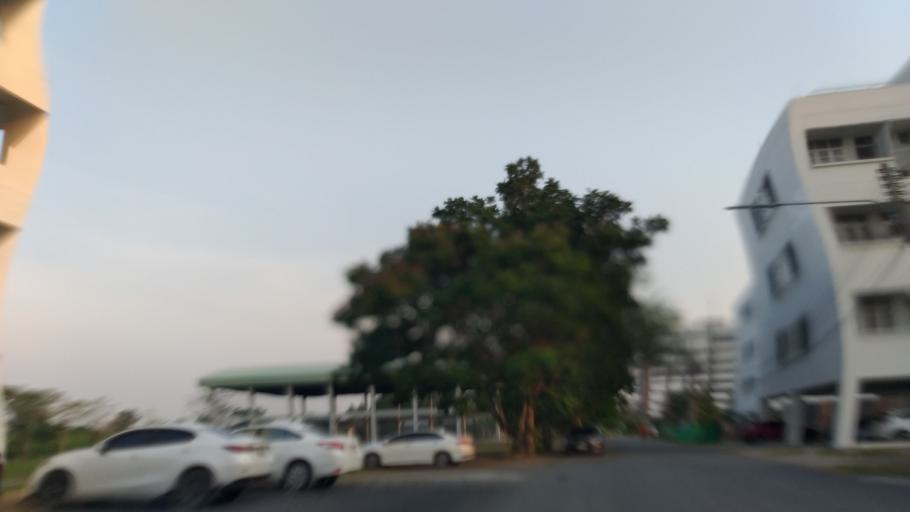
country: TH
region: Pathum Thani
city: Nong Suea
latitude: 14.0716
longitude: 100.8368
